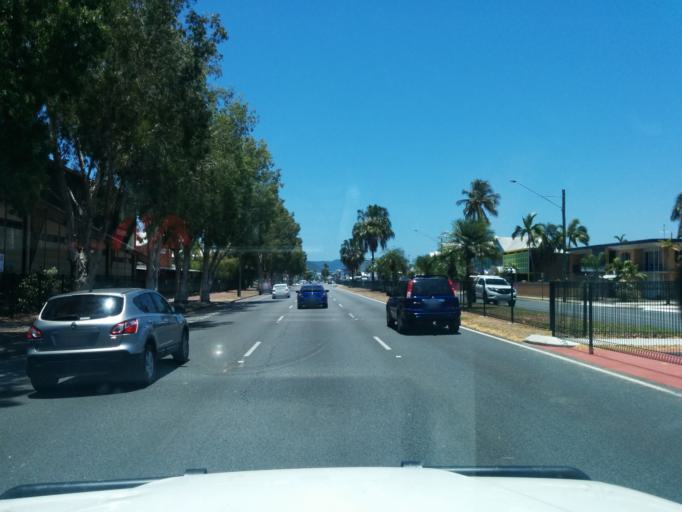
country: AU
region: Queensland
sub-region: Cairns
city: Cairns
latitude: -16.9150
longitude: 145.7664
